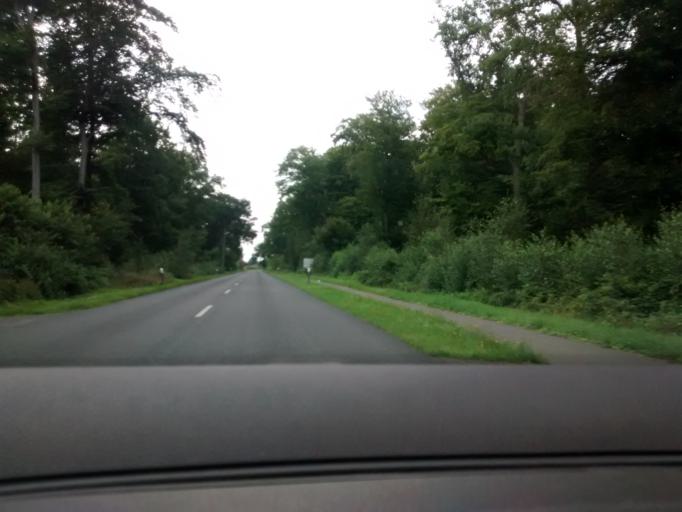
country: DE
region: Lower Saxony
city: Brietlingen
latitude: 53.3229
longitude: 10.4693
